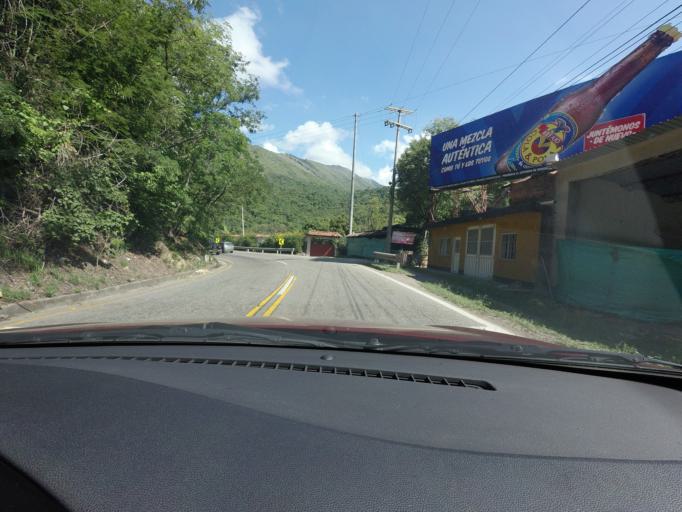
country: CO
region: Cundinamarca
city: Nilo
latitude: 4.2621
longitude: -74.5496
